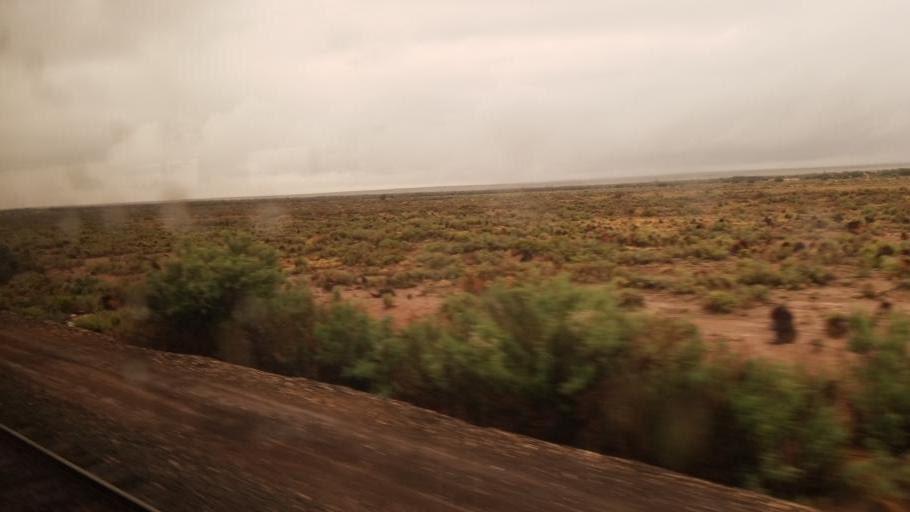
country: US
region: Arizona
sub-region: Navajo County
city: Winslow
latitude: 34.9989
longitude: -110.6242
